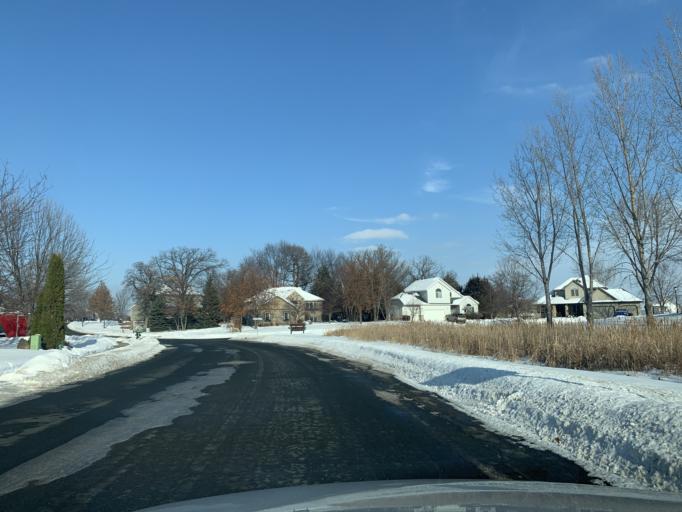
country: US
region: Minnesota
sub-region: Wright County
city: Buffalo
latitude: 45.2025
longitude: -93.8339
